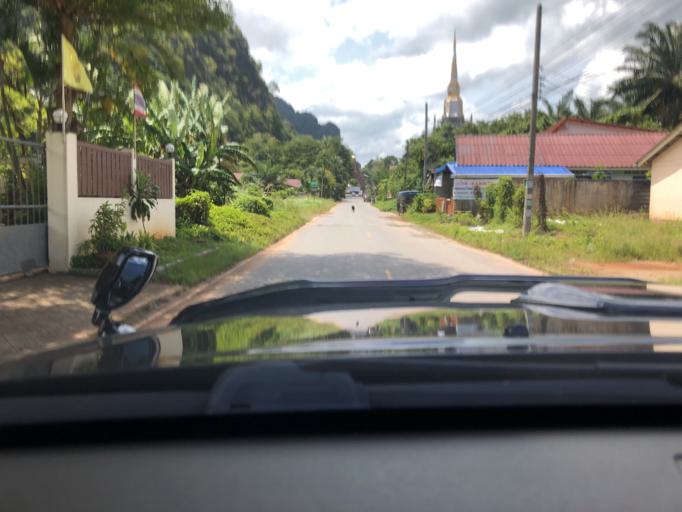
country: TH
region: Krabi
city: Krabi
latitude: 8.1210
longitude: 98.9240
